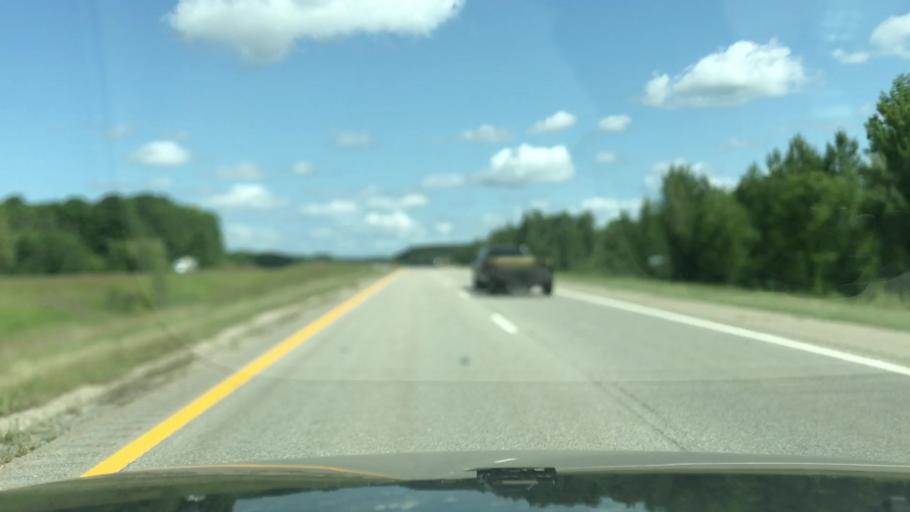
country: US
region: Michigan
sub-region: Mecosta County
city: Big Rapids
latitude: 43.7760
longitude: -85.5340
